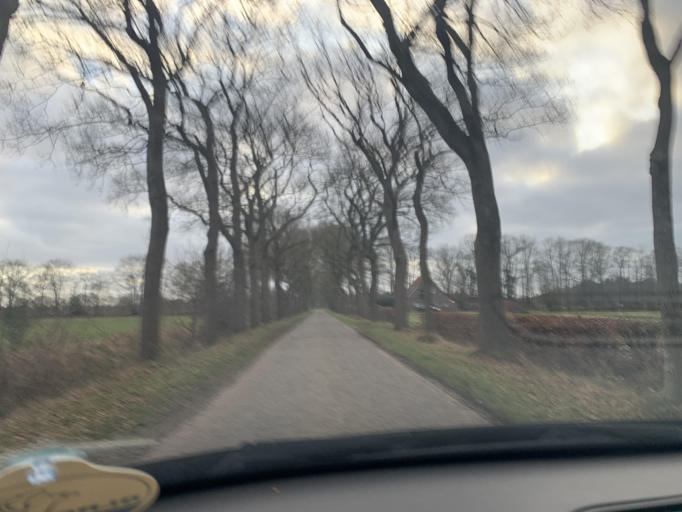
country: DE
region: Lower Saxony
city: Westerstede
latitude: 53.2975
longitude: 7.9303
